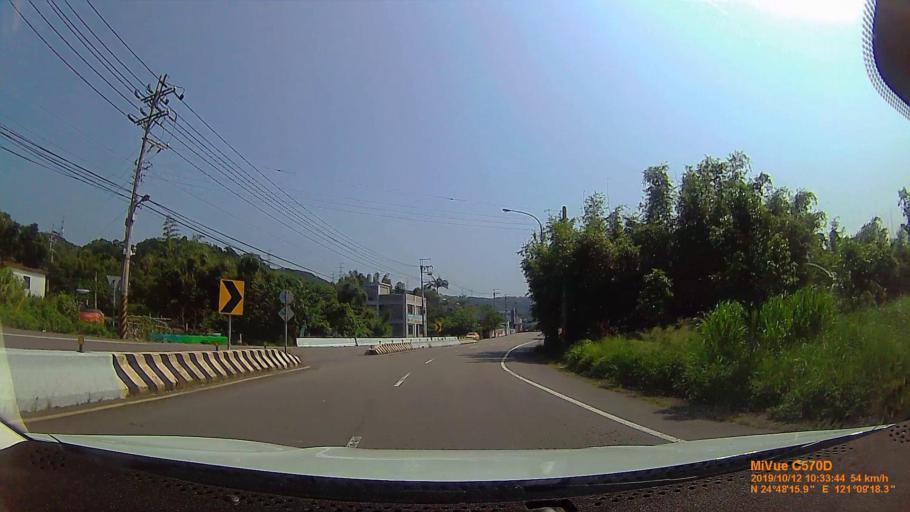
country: TW
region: Taiwan
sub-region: Hsinchu
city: Zhubei
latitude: 24.8044
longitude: 121.1551
